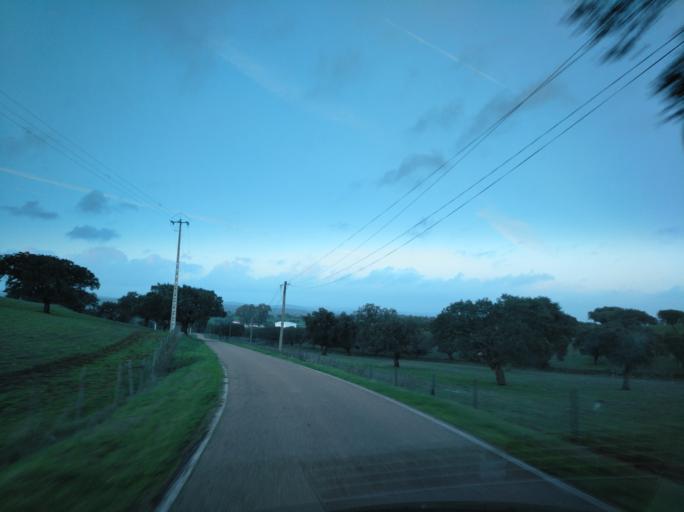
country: PT
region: Portalegre
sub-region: Campo Maior
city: Campo Maior
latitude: 39.0710
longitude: -7.1156
